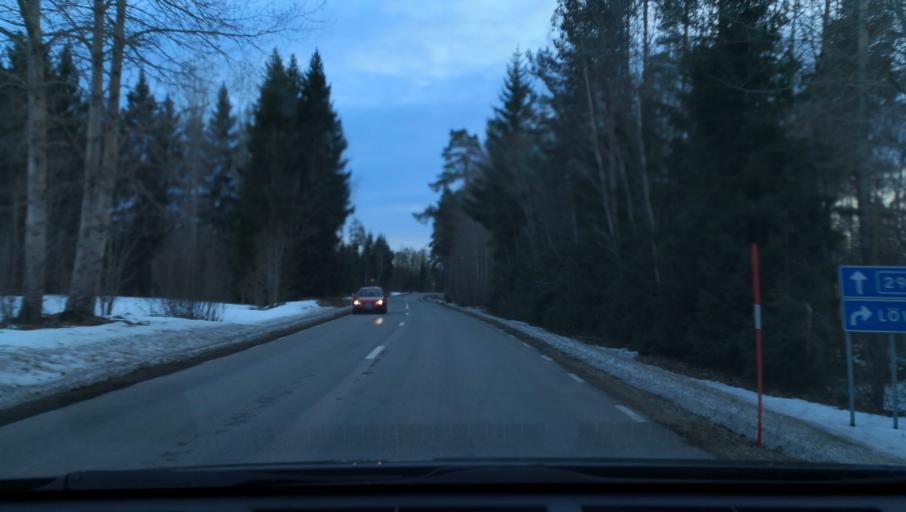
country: SE
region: Uppsala
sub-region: Osthammars Kommun
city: Osterbybruk
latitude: 60.2622
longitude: 17.9521
